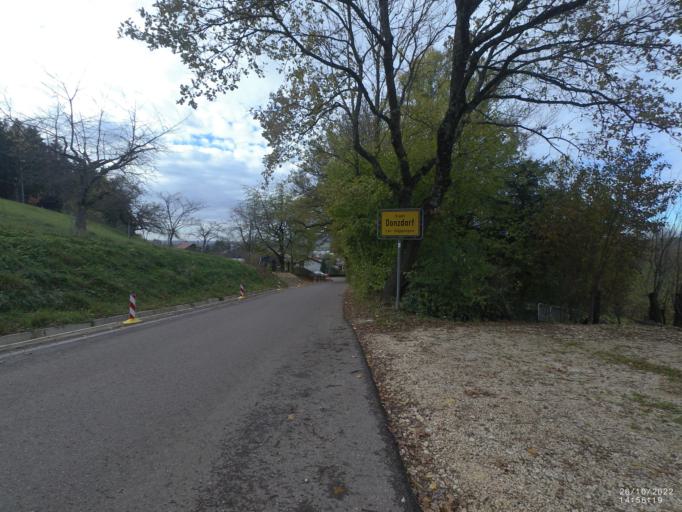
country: DE
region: Baden-Wuerttemberg
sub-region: Regierungsbezirk Stuttgart
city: Donzdorf
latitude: 48.6803
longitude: 9.8120
